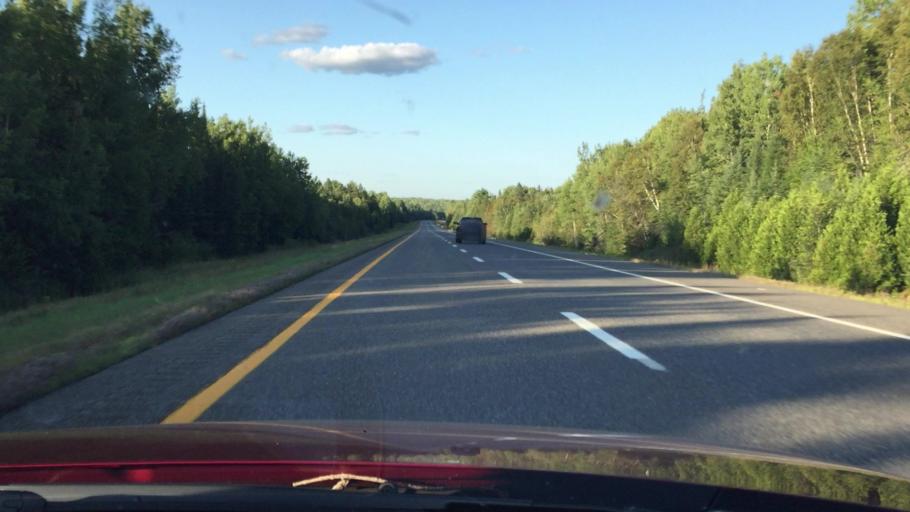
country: US
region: Maine
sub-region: Penobscot County
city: Patten
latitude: 46.0342
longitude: -68.2713
